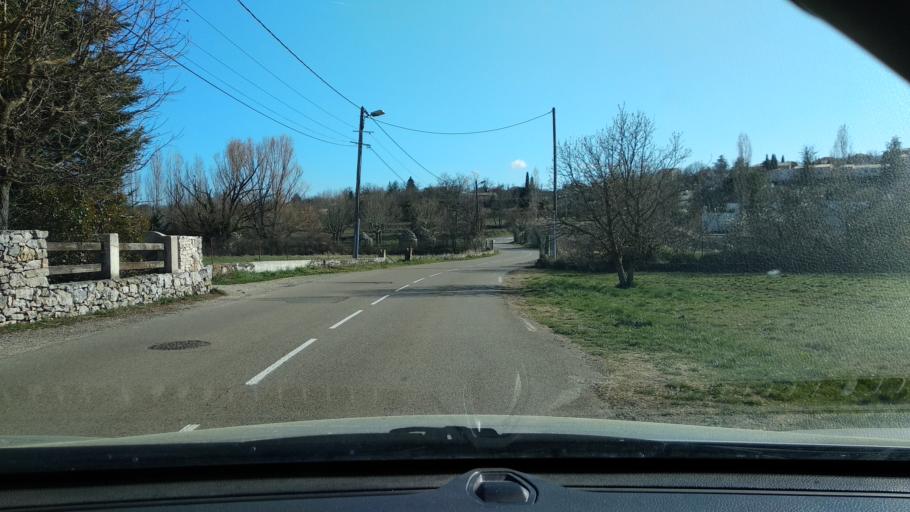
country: FR
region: Provence-Alpes-Cote d'Azur
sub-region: Departement des Alpes-Maritimes
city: Saint-Cezaire-sur-Siagne
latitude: 43.6529
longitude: 6.7976
